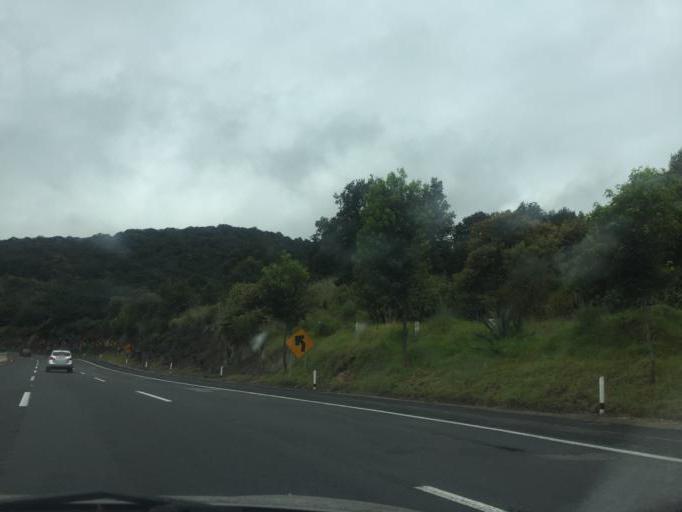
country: MX
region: Mexico City
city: Xochimilco
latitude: 19.2240
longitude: -99.1444
